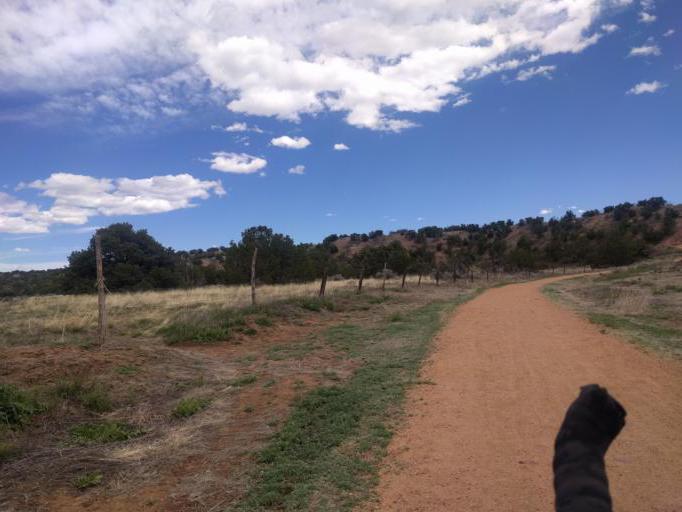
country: US
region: New Mexico
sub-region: Santa Fe County
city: Agua Fria
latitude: 35.6221
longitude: -105.9619
